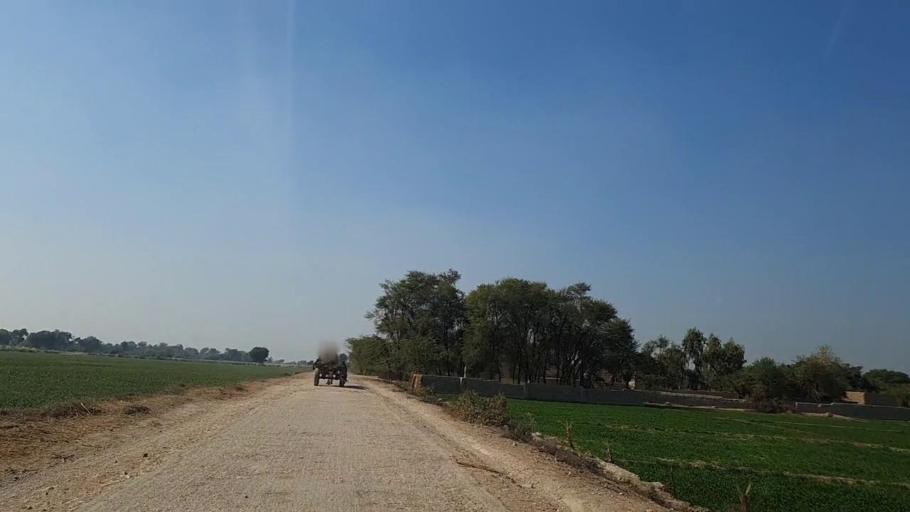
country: PK
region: Sindh
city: Daulatpur
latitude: 26.2906
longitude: 68.0841
